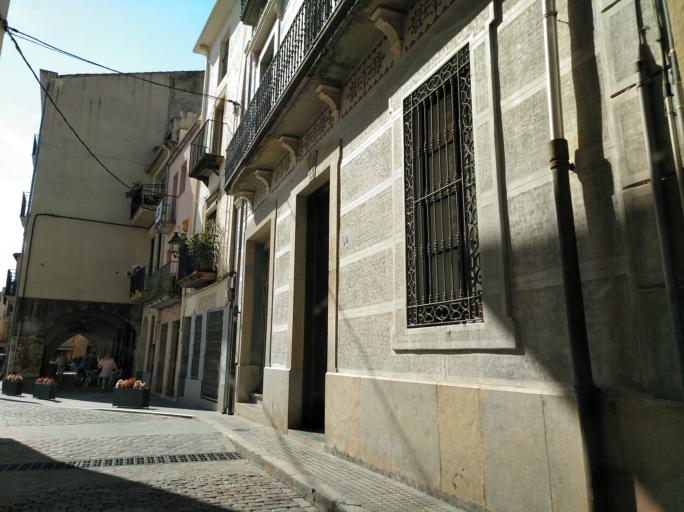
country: ES
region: Catalonia
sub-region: Provincia de Girona
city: la Cellera de Ter
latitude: 42.0092
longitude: 2.6023
